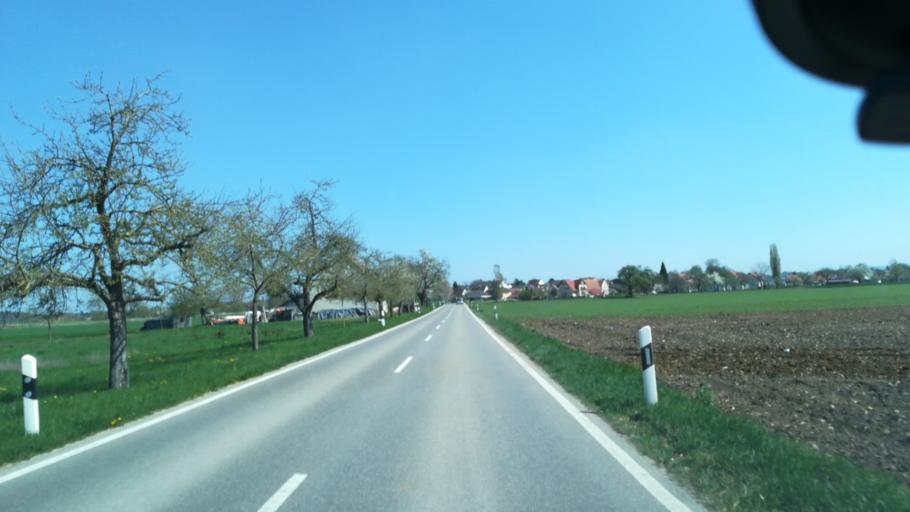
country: DE
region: Baden-Wuerttemberg
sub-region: Freiburg Region
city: Neuhausen
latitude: 47.8296
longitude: 8.7919
